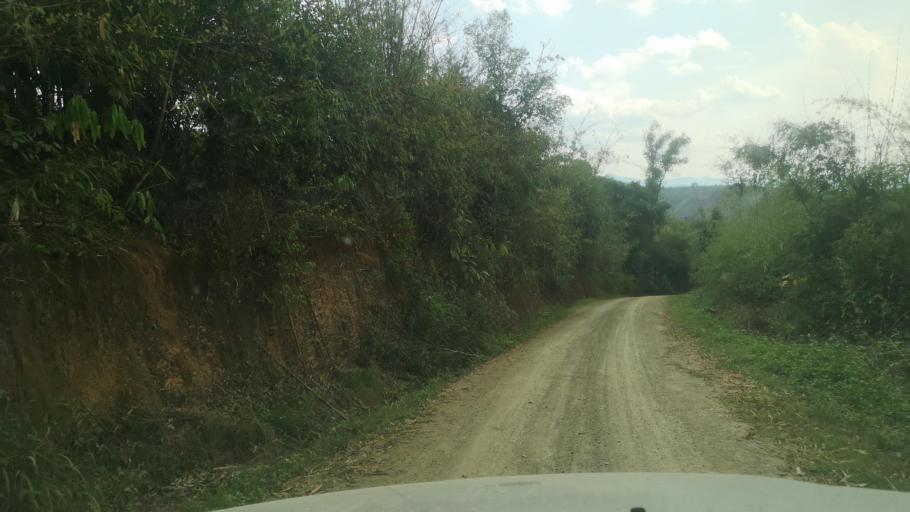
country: LA
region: Loungnamtha
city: Muang Nale
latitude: 20.3037
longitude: 101.3456
